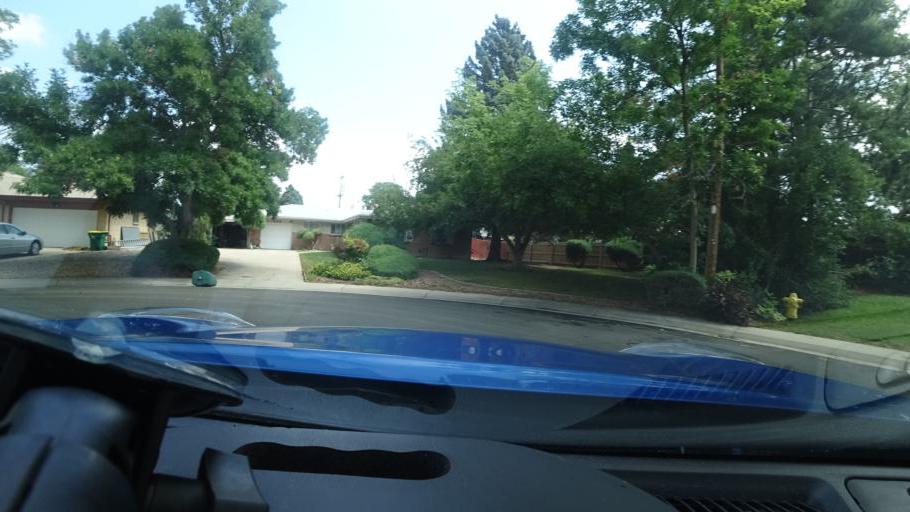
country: US
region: Colorado
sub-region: Adams County
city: Aurora
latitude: 39.7204
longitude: -104.8569
